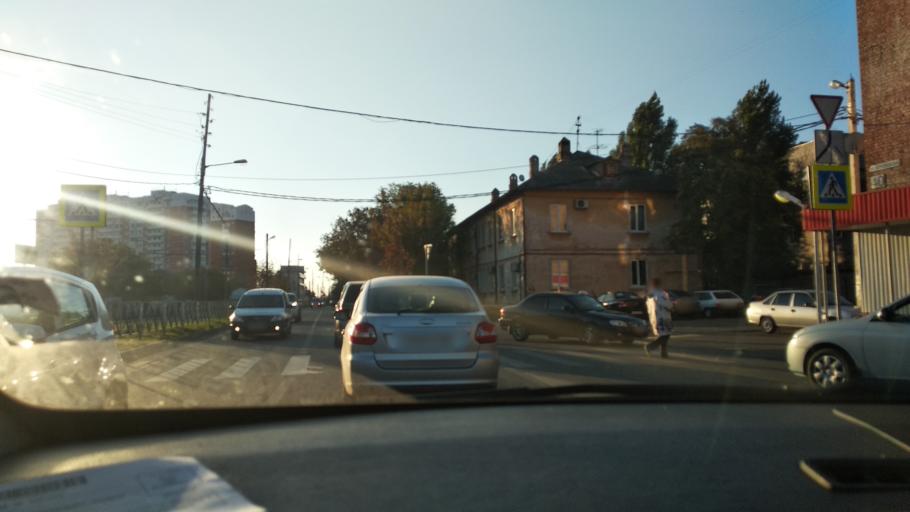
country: RU
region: Krasnodarskiy
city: Krasnodar
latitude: 45.0064
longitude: 39.0167
